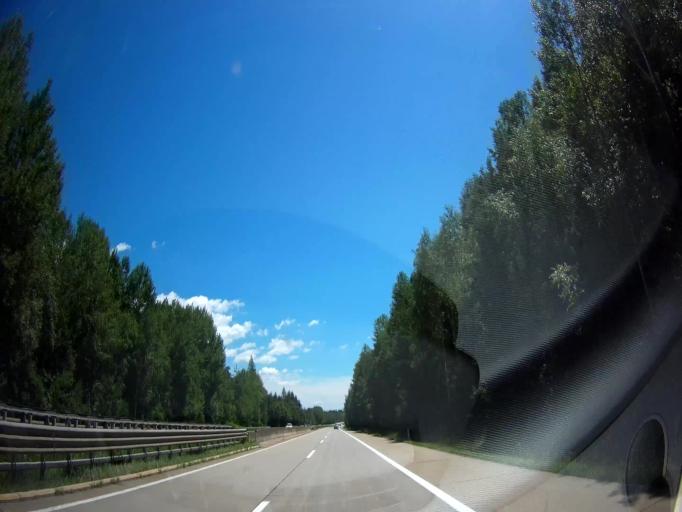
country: AT
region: Carinthia
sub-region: Politischer Bezirk Villach Land
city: Ferndorf
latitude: 46.7325
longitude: 13.5985
